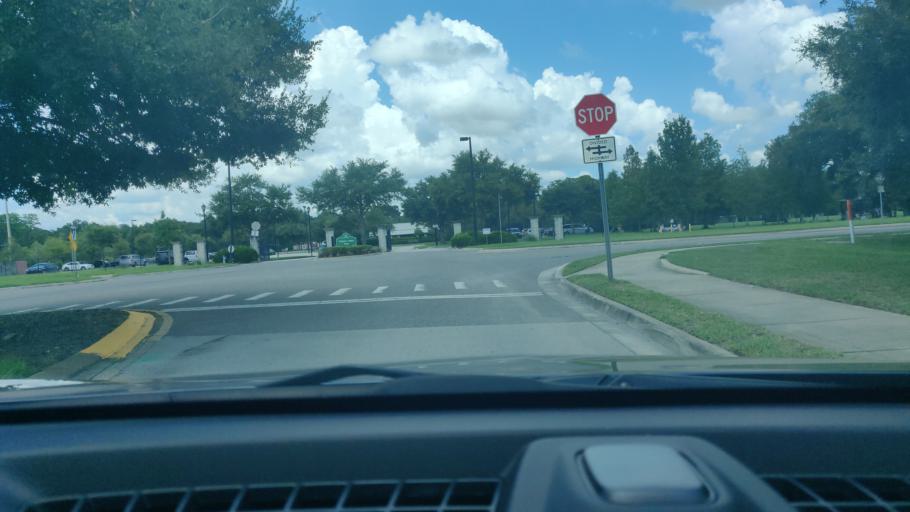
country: US
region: Florida
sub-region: Orange County
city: Belle Isle
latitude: 28.4607
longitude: -81.3143
